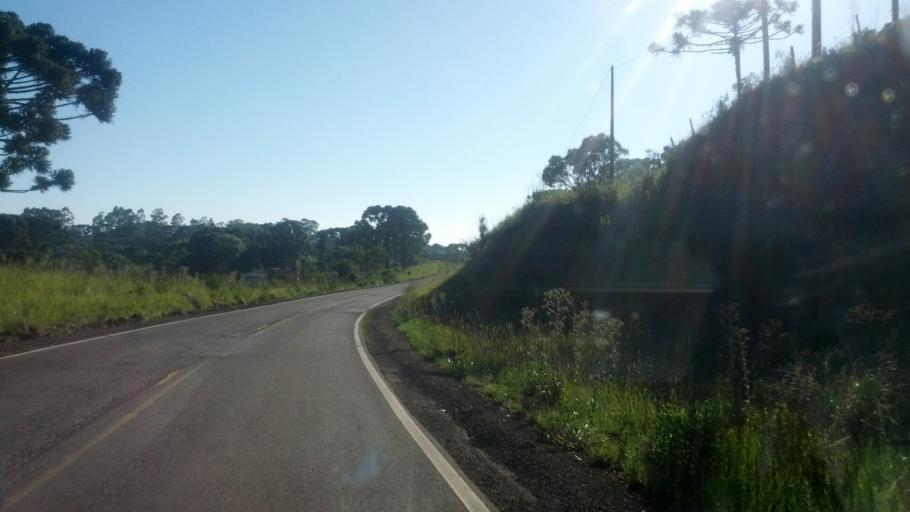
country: BR
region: Santa Catarina
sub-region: Lages
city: Lages
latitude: -27.9135
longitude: -50.5828
